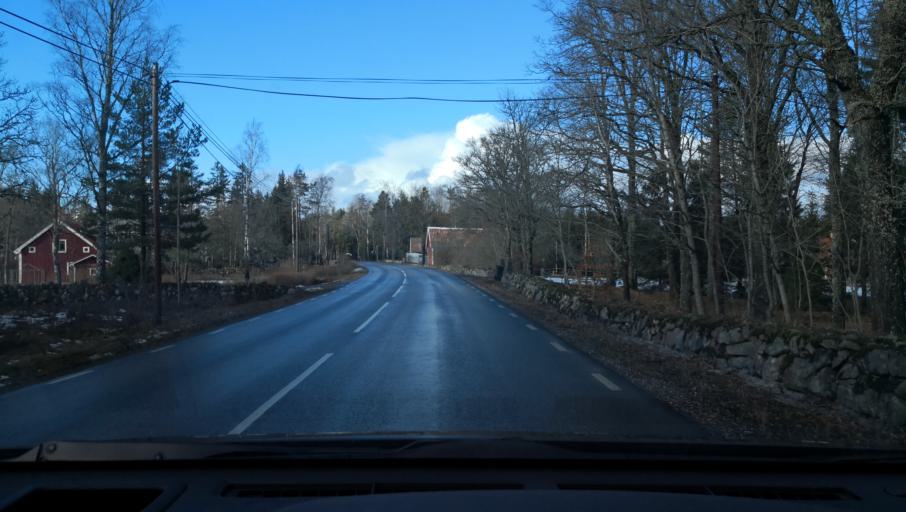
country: SE
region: Vaestmanland
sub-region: Arboga Kommun
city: Arboga
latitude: 59.3706
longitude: 15.8450
